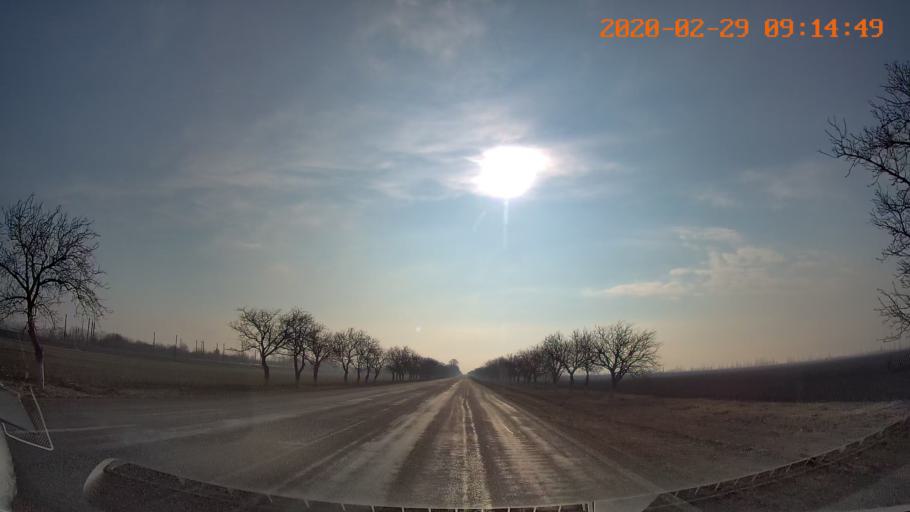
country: MD
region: Telenesti
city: Pervomaisc
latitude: 46.8055
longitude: 29.8592
